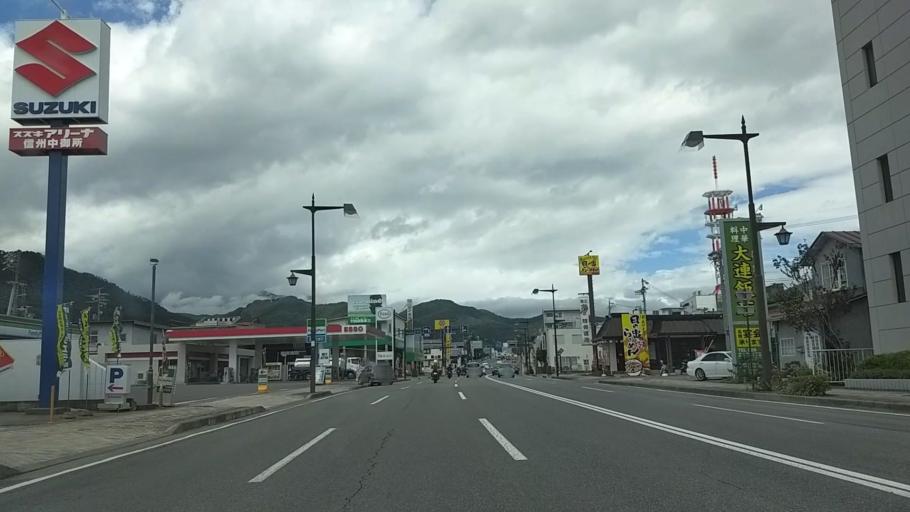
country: JP
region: Nagano
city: Nagano-shi
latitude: 36.6354
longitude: 138.1819
